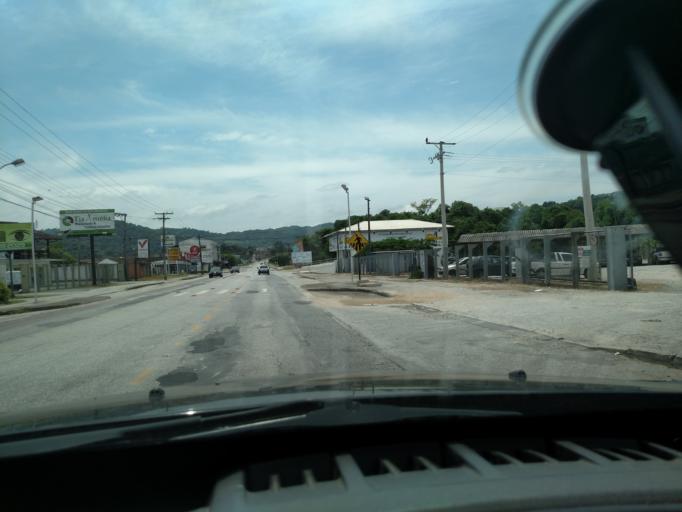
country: BR
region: Santa Catarina
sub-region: Gaspar
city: Gaspar
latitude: -26.8981
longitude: -49.0071
